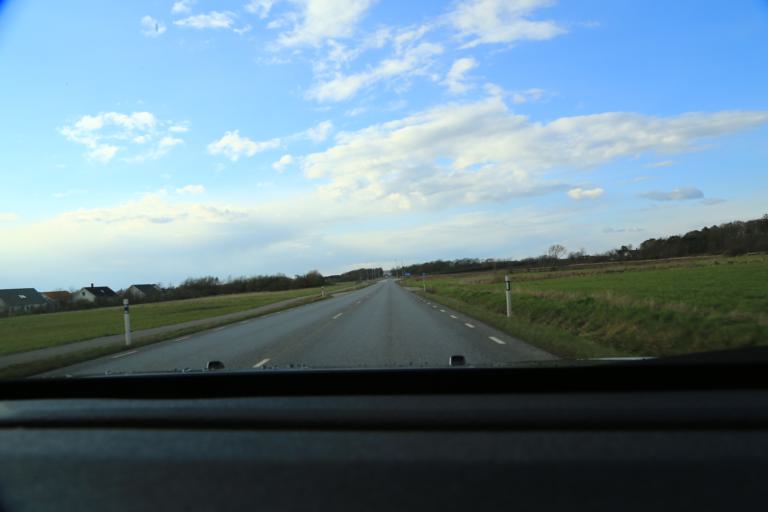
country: SE
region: Halland
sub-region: Varbergs Kommun
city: Traslovslage
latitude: 57.0609
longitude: 12.2961
